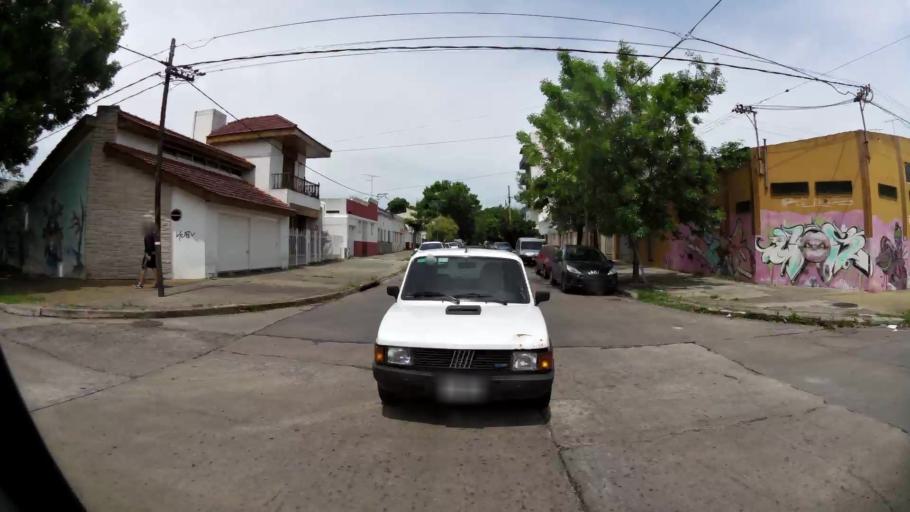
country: AR
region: Buenos Aires
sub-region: Partido de La Plata
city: La Plata
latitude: -34.9409
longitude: -57.9511
